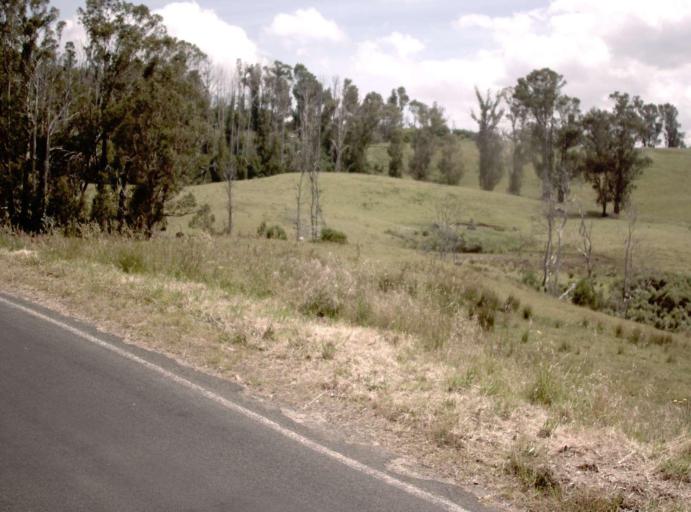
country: AU
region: Victoria
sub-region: Latrobe
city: Traralgon
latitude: -38.3273
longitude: 146.5741
